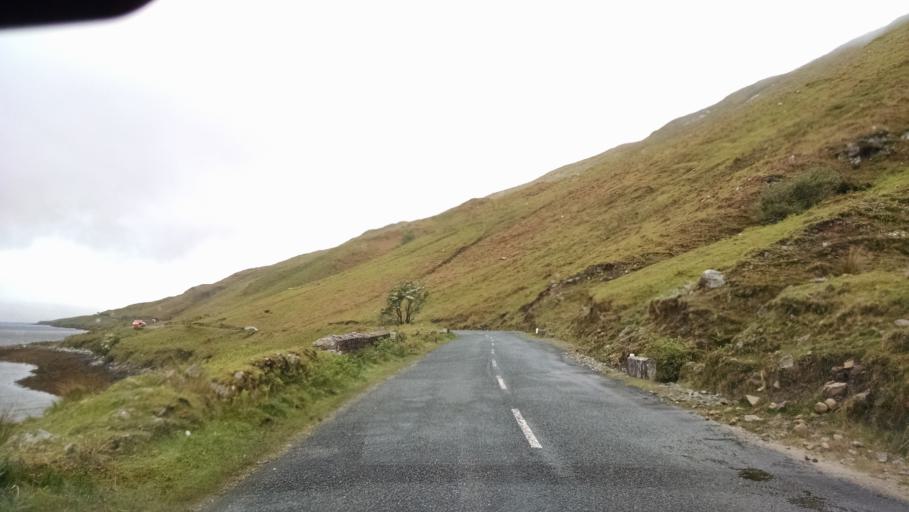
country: IE
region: Connaught
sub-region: Maigh Eo
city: Westport
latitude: 53.6050
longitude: -9.7038
